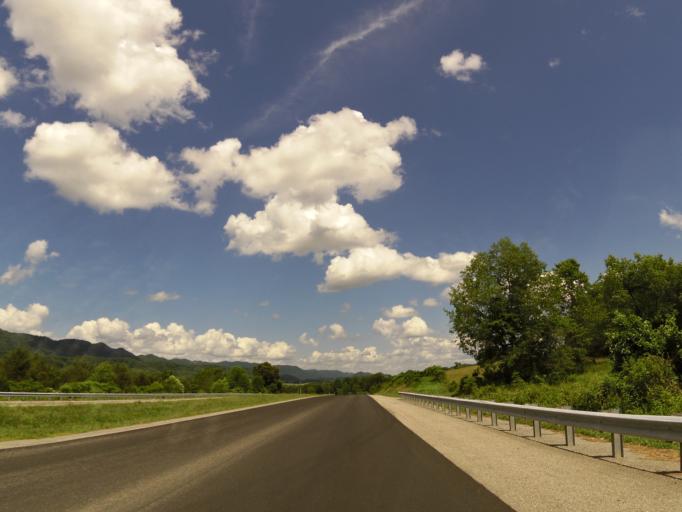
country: US
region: Virginia
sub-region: Lee County
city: Jonesville
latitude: 36.6975
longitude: -83.2630
